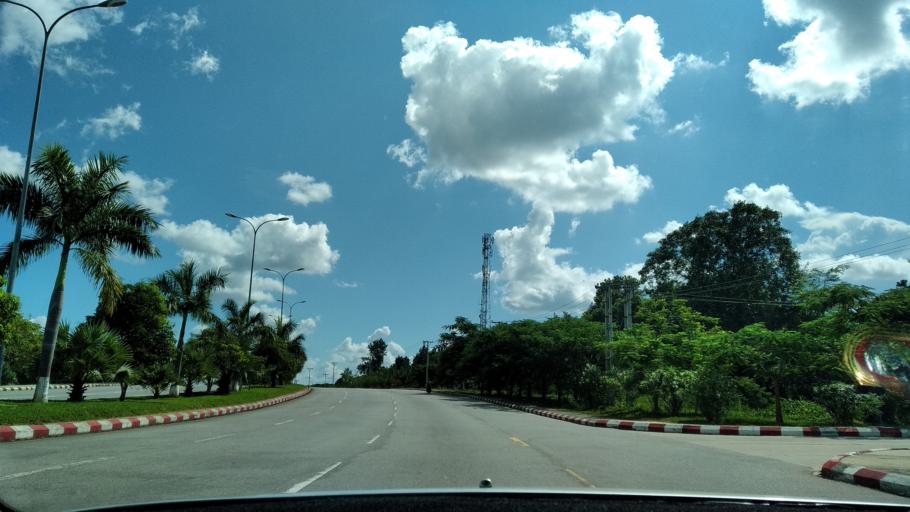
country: MM
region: Mandalay
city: Nay Pyi Taw
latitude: 19.7900
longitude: 96.1451
